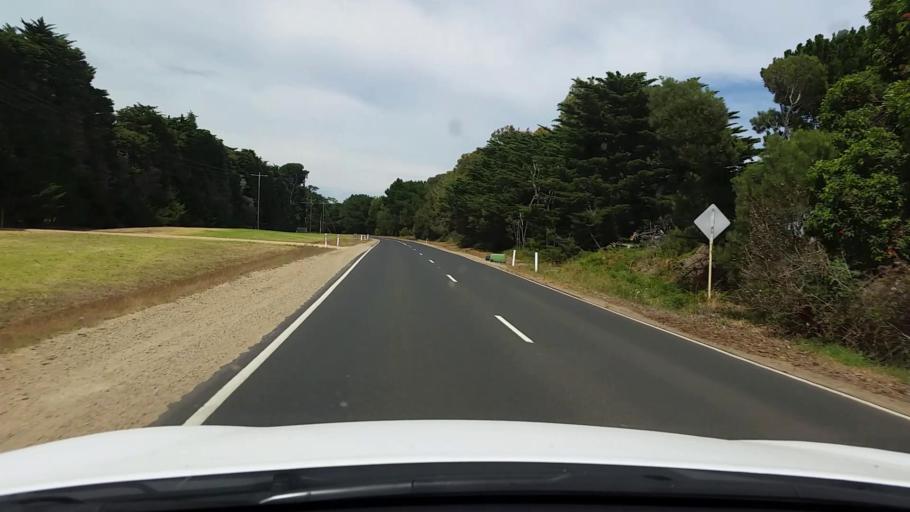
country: AU
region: Victoria
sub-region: Mornington Peninsula
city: Merricks
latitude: -38.4544
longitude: 145.0201
